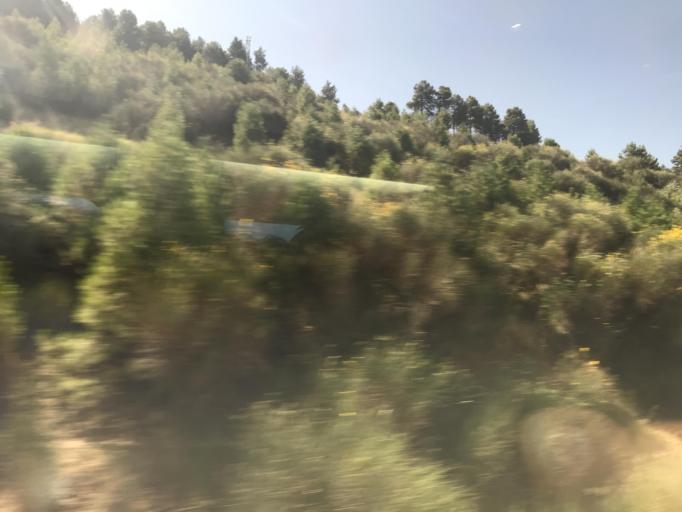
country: ES
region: Castille and Leon
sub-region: Provincia de Burgos
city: Villalbilla de Burgos
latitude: 42.3626
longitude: -3.7484
